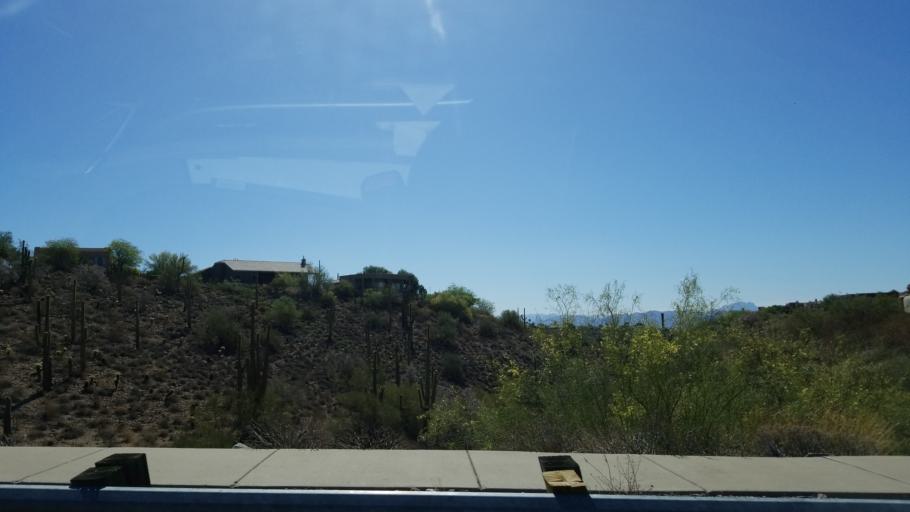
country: US
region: Arizona
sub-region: Maricopa County
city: Fountain Hills
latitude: 33.5915
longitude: -111.7558
